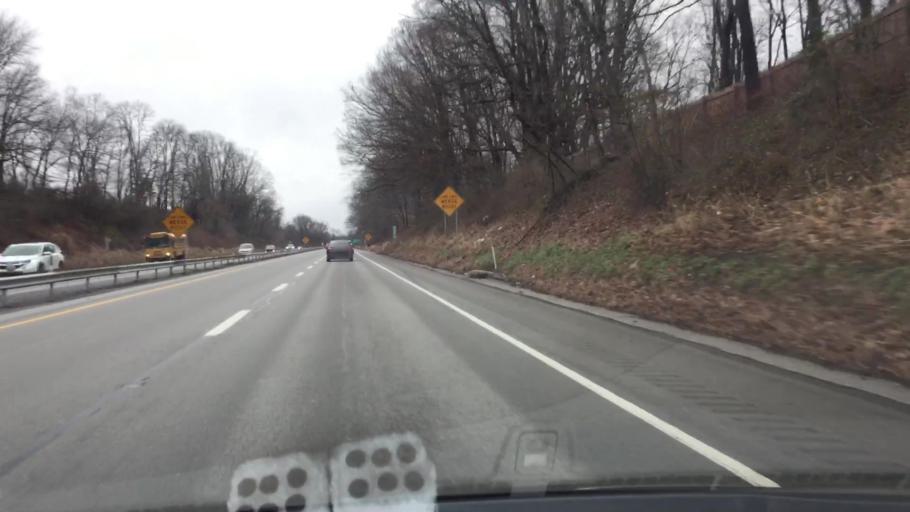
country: US
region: Pennsylvania
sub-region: Delaware County
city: Media
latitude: 39.9225
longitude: -75.4133
